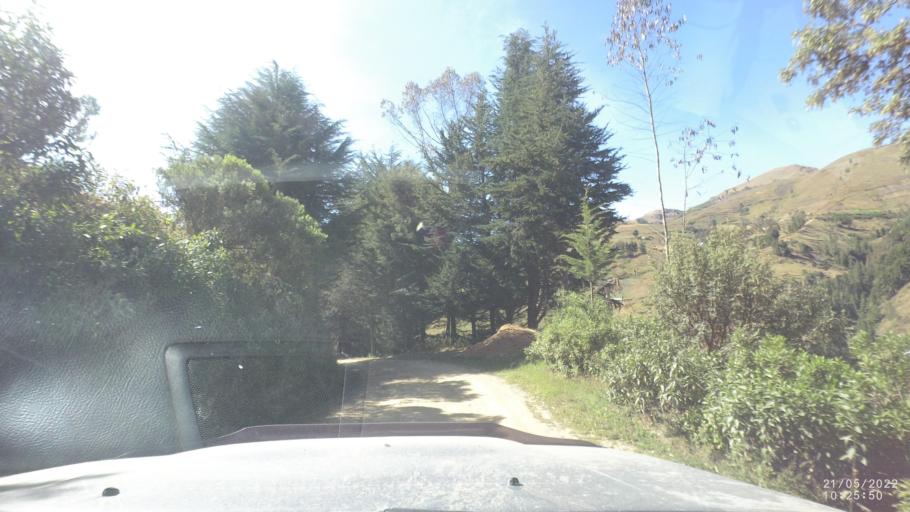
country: BO
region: Cochabamba
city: Colomi
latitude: -17.3258
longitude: -65.9488
